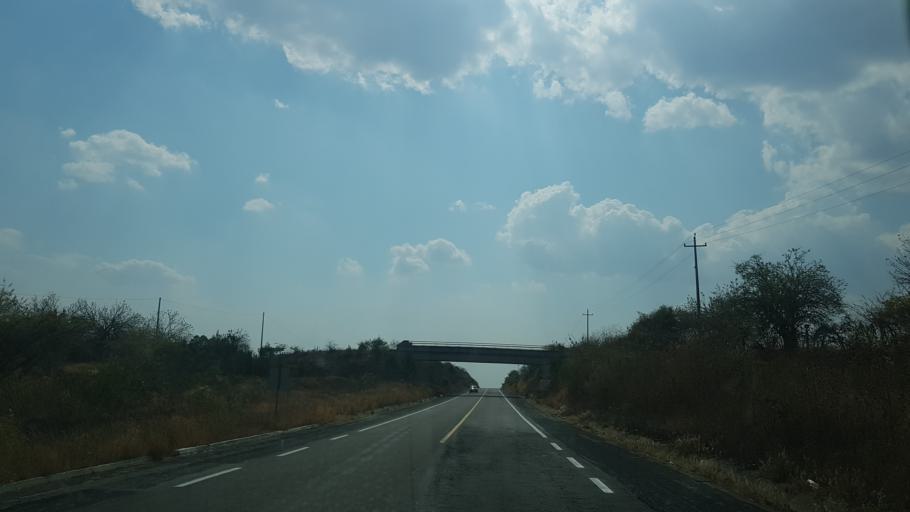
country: MX
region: Puebla
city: San Juan Amecac
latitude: 18.8165
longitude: -98.6620
